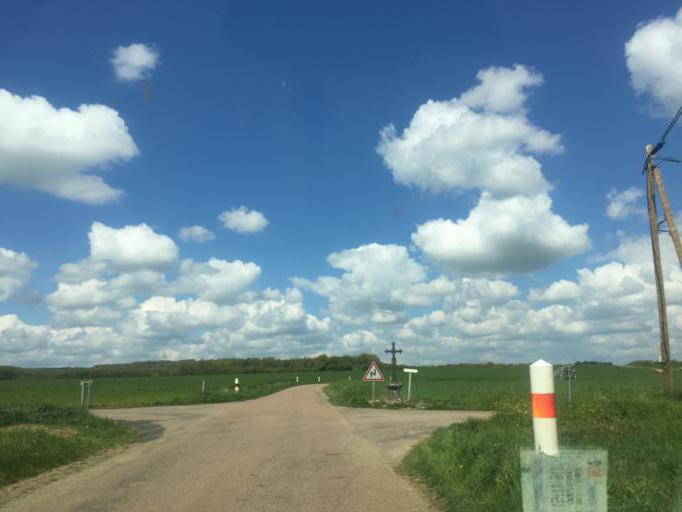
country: FR
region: Bourgogne
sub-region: Departement de l'Yonne
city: Fontenailles
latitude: 47.5290
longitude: 3.3445
